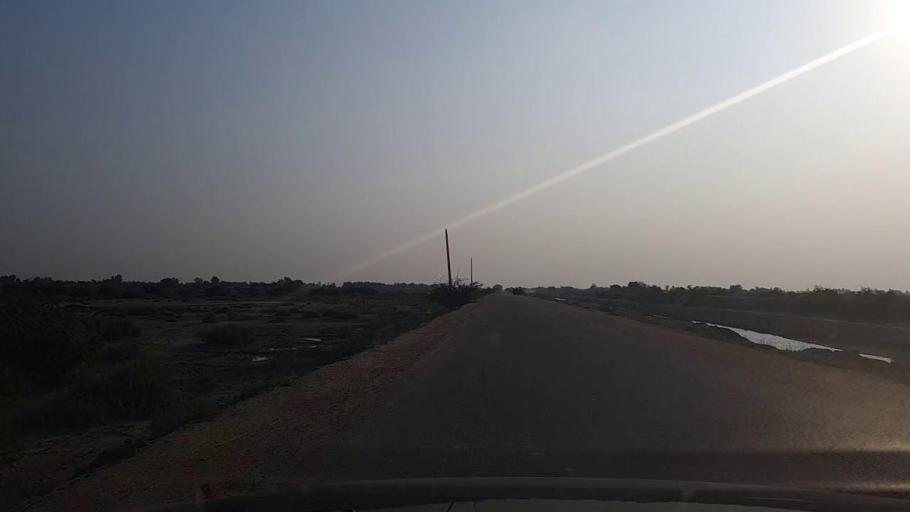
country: PK
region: Sindh
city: Mirpur Sakro
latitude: 24.5095
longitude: 67.8181
